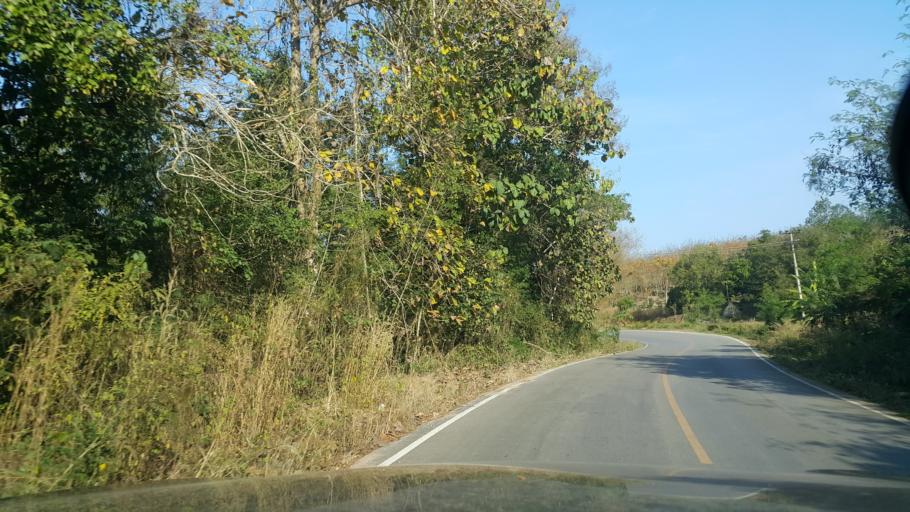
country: TH
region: Loei
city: Chiang Khan
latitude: 17.8136
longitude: 101.6284
